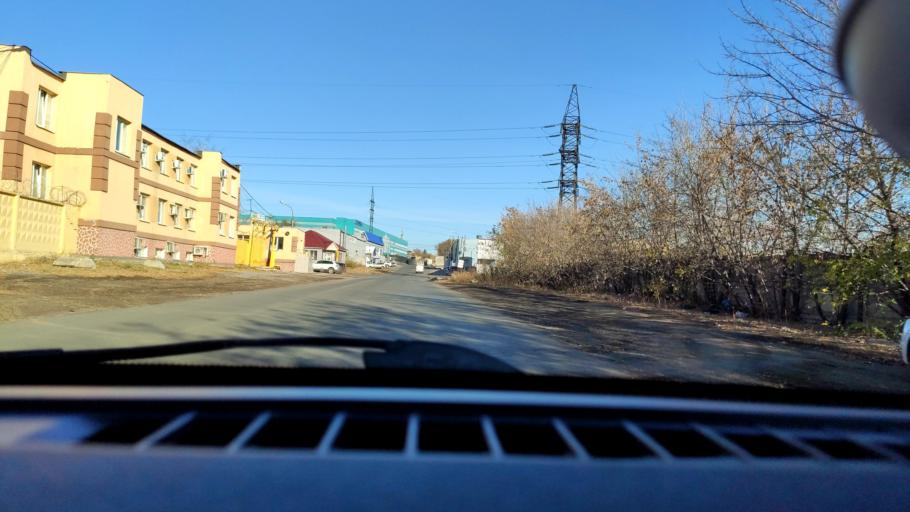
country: RU
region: Samara
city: Samara
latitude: 53.1813
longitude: 50.1705
